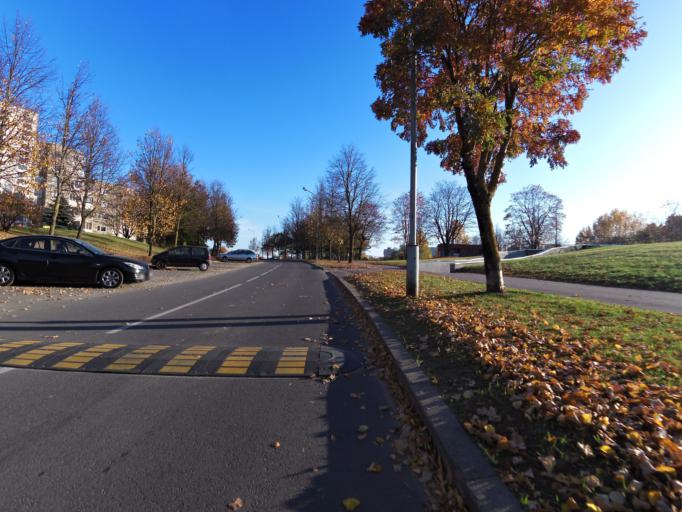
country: LT
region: Vilnius County
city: Pasilaiciai
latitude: 54.7266
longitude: 25.2201
